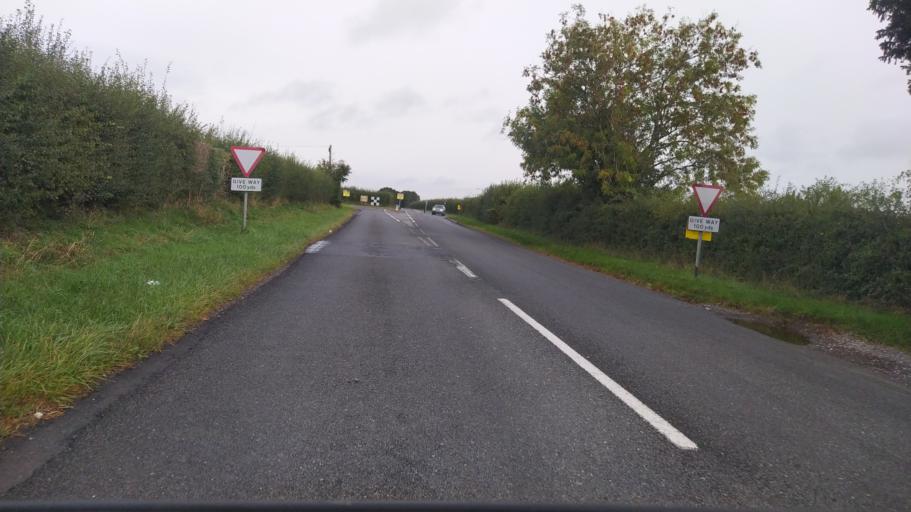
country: GB
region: England
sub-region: Hampshire
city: East Dean
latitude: 51.1112
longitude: -1.5773
